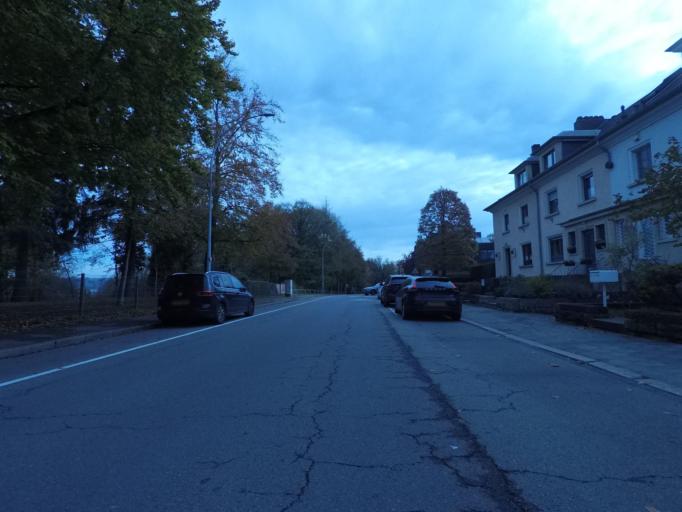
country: LU
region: Luxembourg
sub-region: Canton de Luxembourg
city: Luxembourg
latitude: 49.6247
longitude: 6.1234
